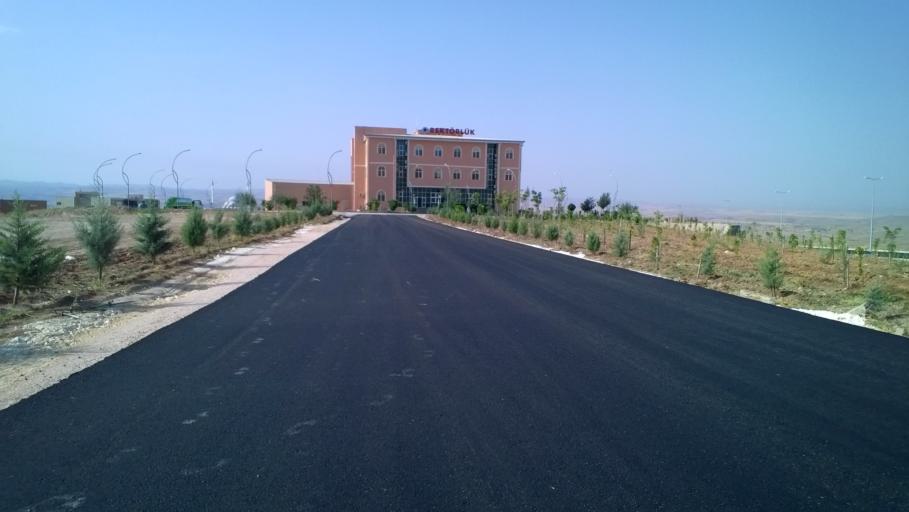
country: TR
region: Batman
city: Oymatas
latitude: 37.7951
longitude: 41.0637
